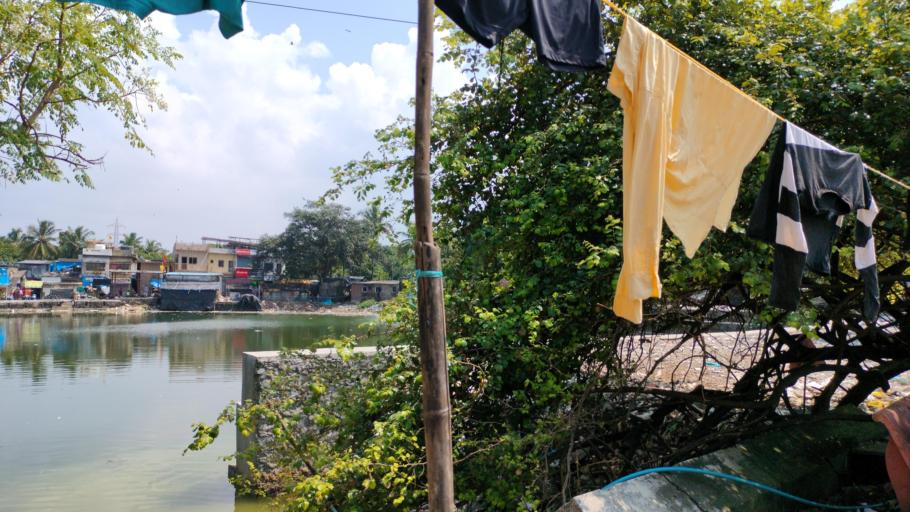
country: IN
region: Maharashtra
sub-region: Mumbai Suburban
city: Borivli
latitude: 19.1461
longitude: 72.7984
